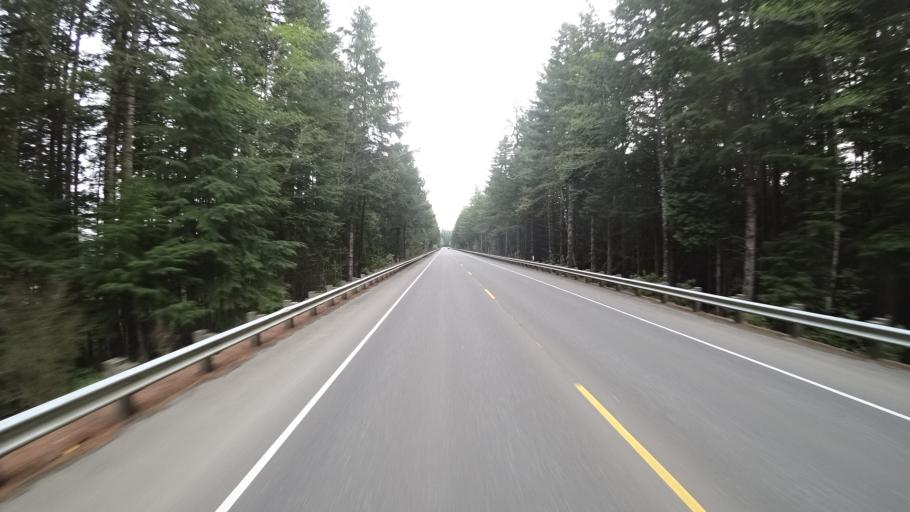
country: US
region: Oregon
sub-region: Coos County
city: Barview
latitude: 43.2469
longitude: -124.2869
